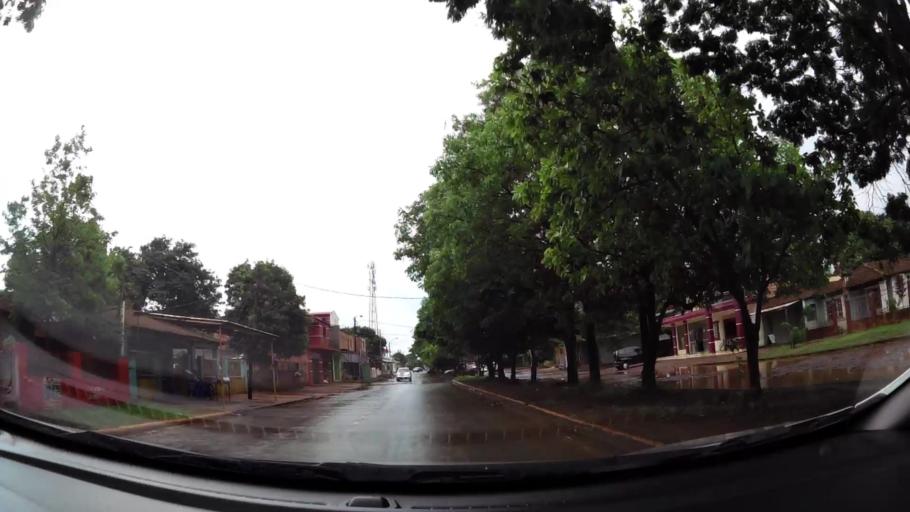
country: PY
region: Alto Parana
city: Presidente Franco
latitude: -25.5218
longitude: -54.6647
